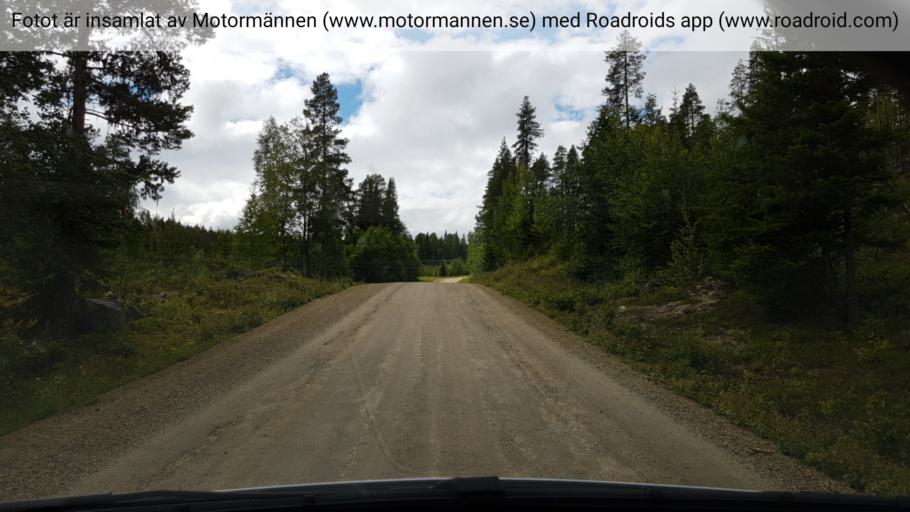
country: SE
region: Vaesterbotten
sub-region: Lycksele Kommun
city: Lycksele
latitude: 64.6015
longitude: 19.1337
